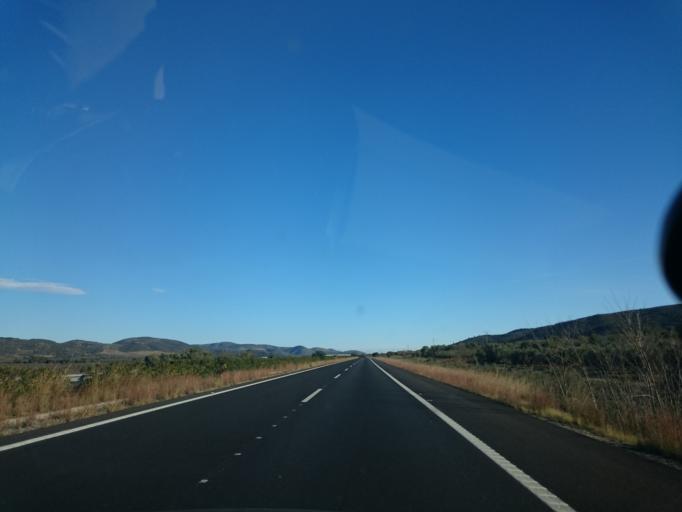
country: ES
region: Valencia
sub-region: Provincia de Castello
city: Alcala de Xivert
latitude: 40.3135
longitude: 0.2451
